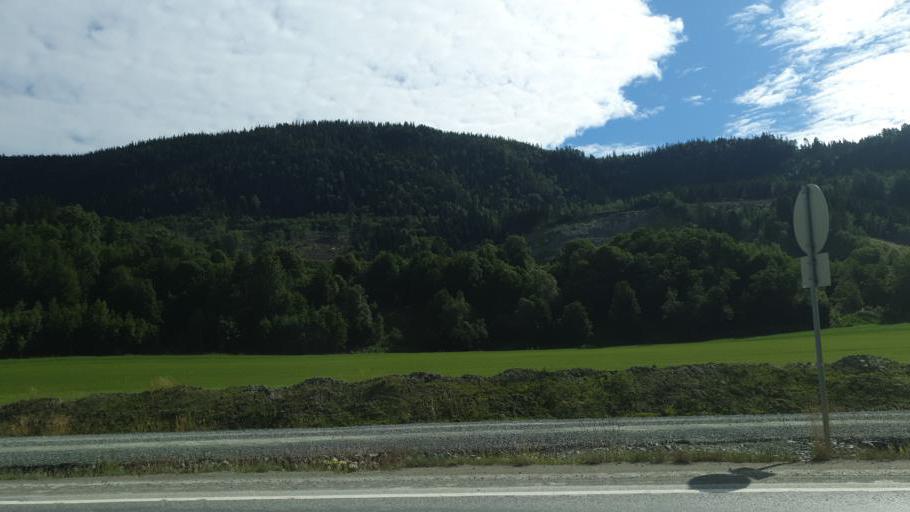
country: NO
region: Sor-Trondelag
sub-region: Melhus
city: Melhus
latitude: 63.2416
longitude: 10.2764
